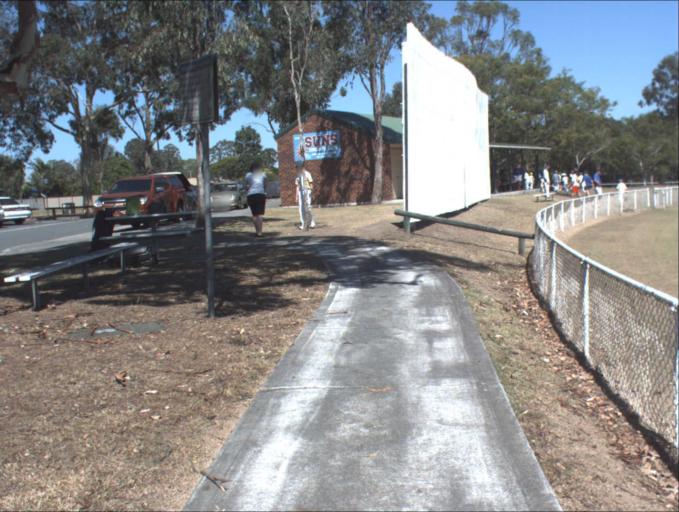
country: AU
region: Queensland
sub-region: Gold Coast
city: Yatala
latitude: -27.7086
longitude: 153.2256
